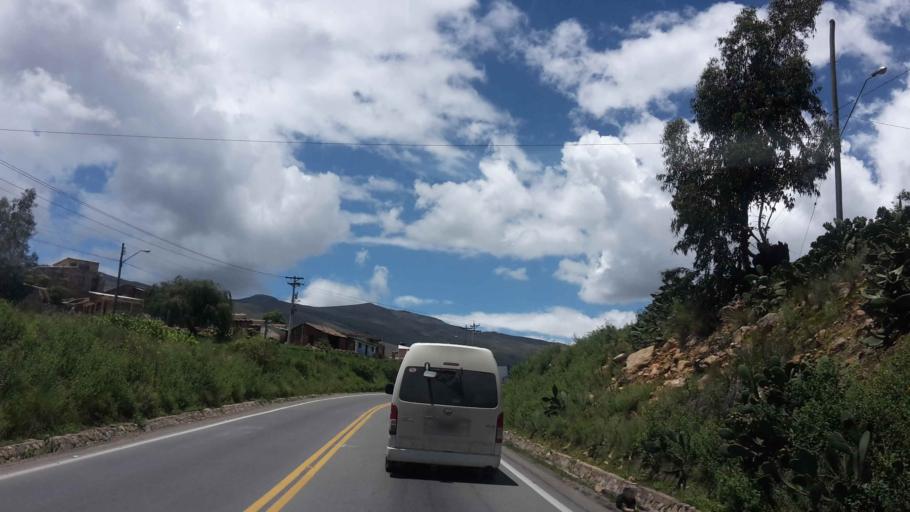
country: BO
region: Cochabamba
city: Colomi
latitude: -17.4206
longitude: -65.9272
